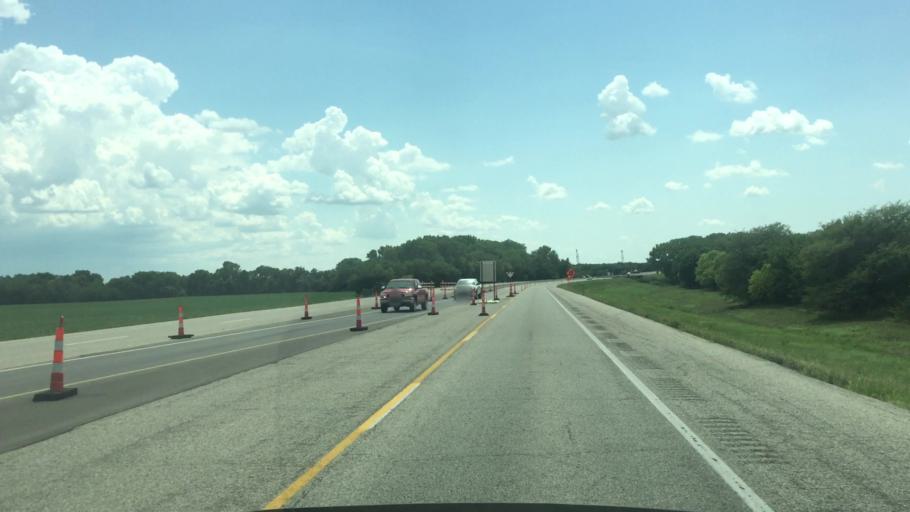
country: US
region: Kansas
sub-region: Lyon County
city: Emporia
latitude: 38.4583
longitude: -96.1950
